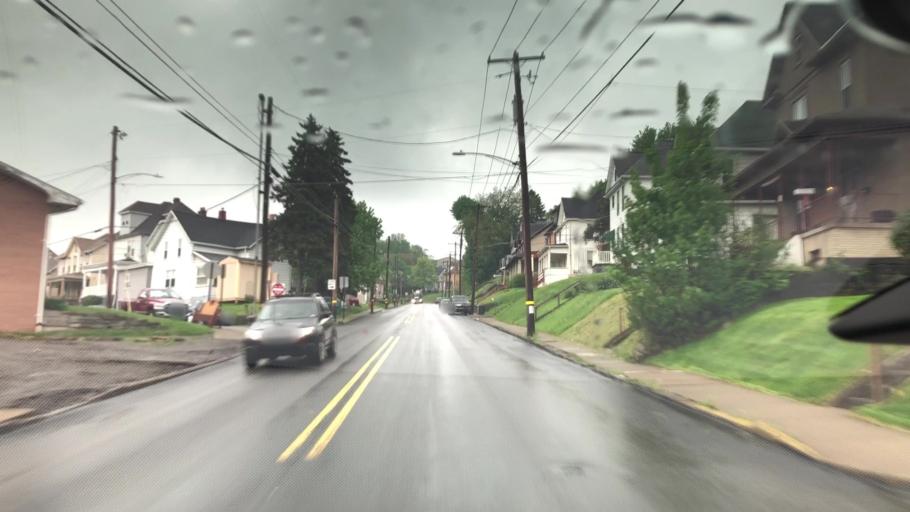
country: US
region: Pennsylvania
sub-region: Butler County
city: Butler
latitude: 40.8535
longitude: -79.8863
